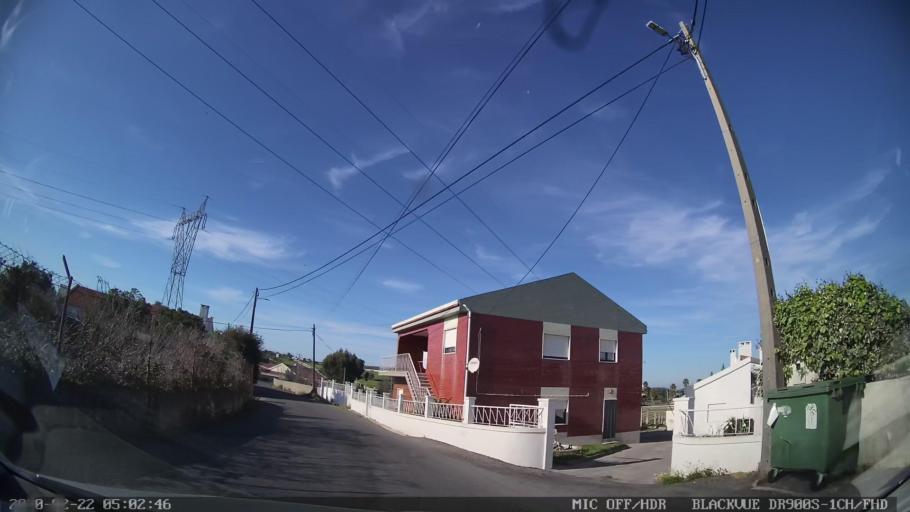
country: PT
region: Lisbon
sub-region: Vila Franca de Xira
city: Vila Franca de Xira
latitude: 38.9662
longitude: -8.9955
